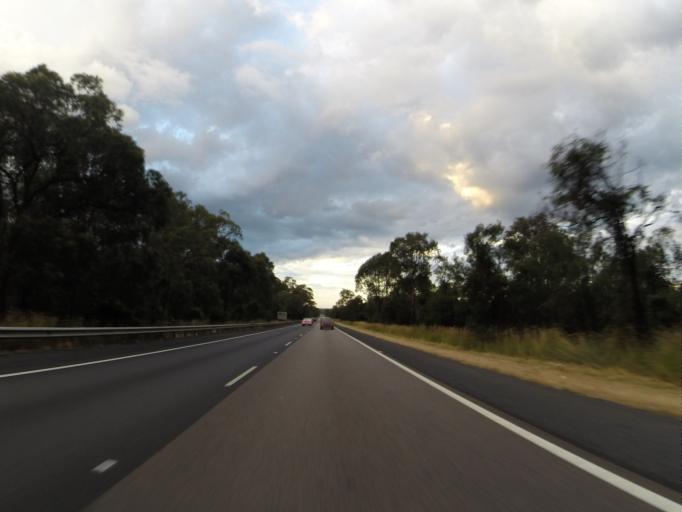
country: AU
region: New South Wales
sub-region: Wollondilly
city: Douglas Park
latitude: -34.2127
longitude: 150.6873
